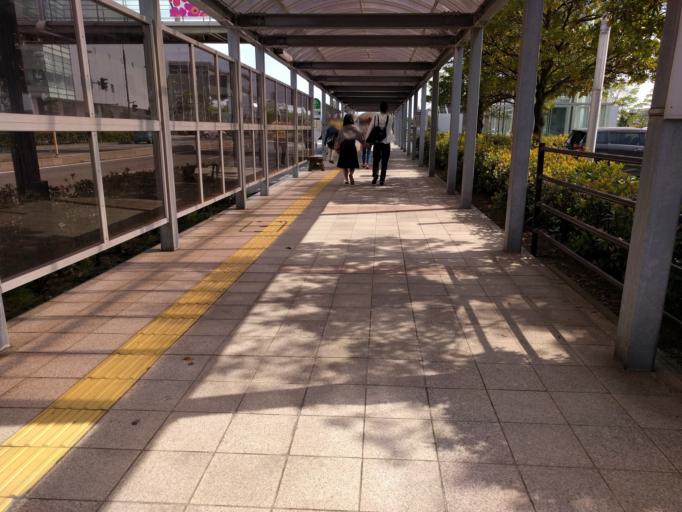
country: JP
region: Niigata
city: Niigata-shi
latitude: 37.9249
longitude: 139.0601
